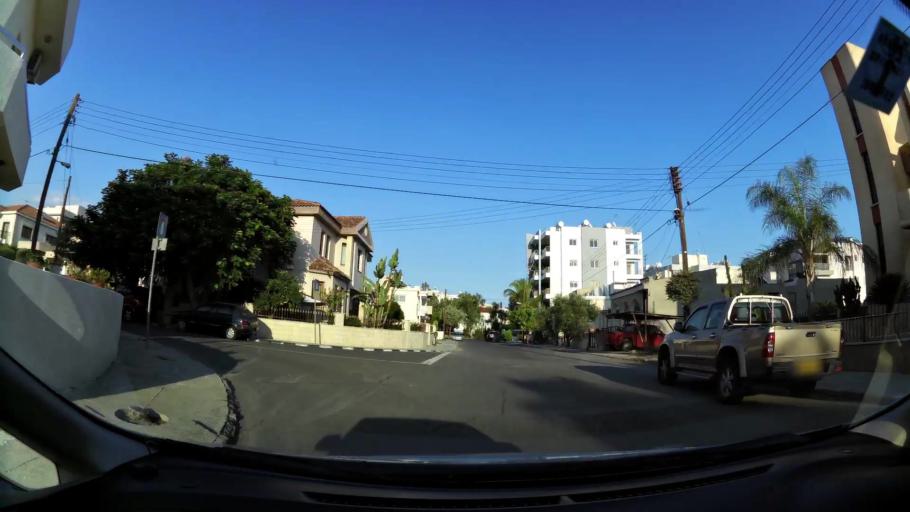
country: CY
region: Larnaka
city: Larnaca
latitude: 34.9203
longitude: 33.5988
